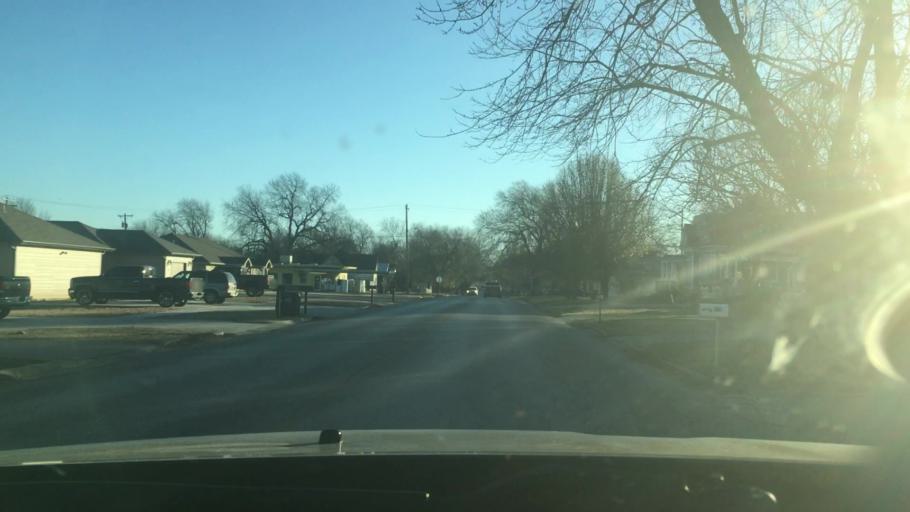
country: US
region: Oklahoma
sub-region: Pontotoc County
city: Ada
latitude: 34.7713
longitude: -96.6862
